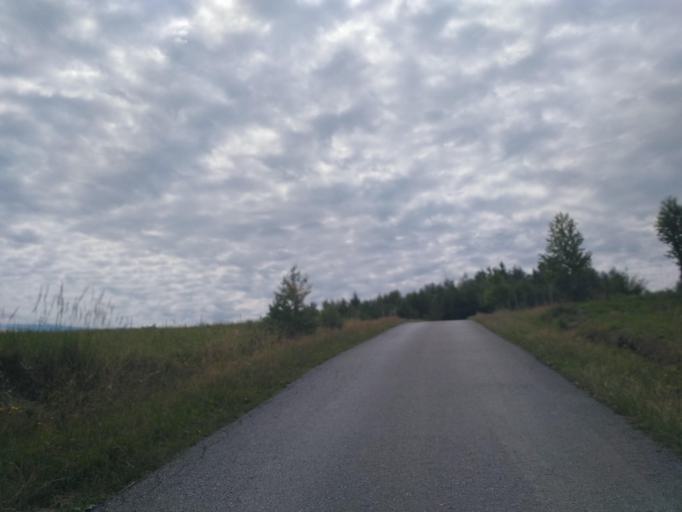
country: PL
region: Subcarpathian Voivodeship
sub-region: Powiat rzeszowski
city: Straszydle
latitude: 49.8911
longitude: 21.9815
